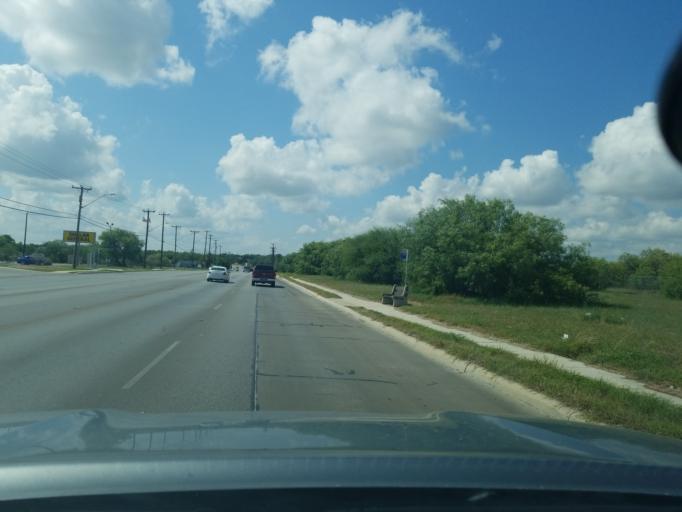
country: US
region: Texas
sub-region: Bexar County
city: San Antonio
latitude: 29.3382
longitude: -98.5342
